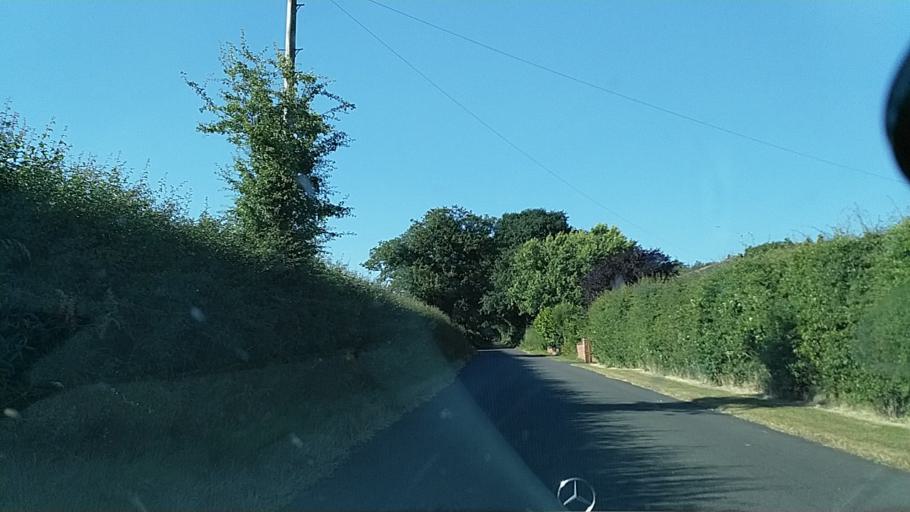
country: GB
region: England
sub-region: Warwickshire
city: Wroxall
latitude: 52.3409
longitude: -1.6559
